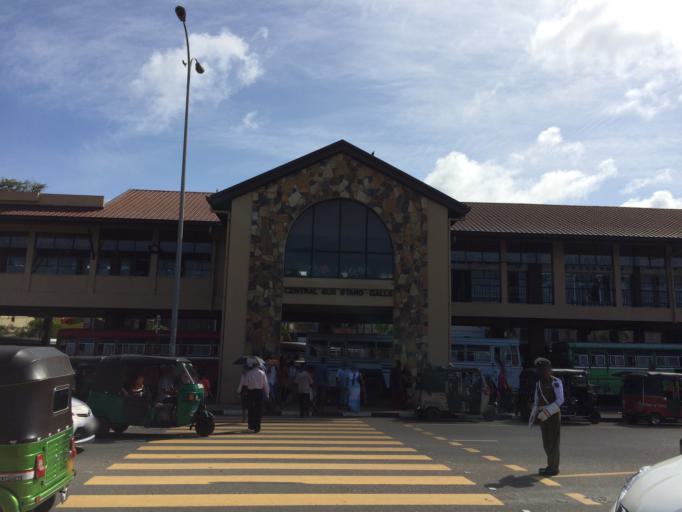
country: LK
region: Southern
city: Galle
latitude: 6.0328
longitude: 80.2153
